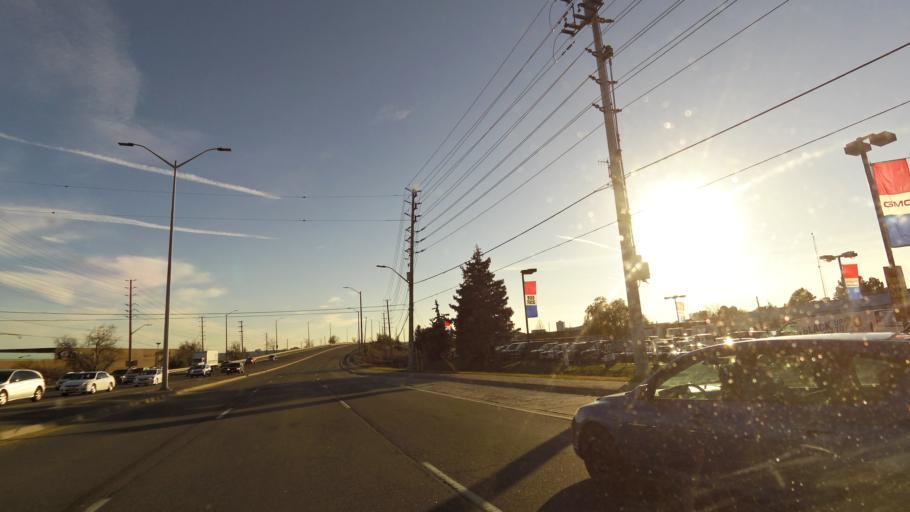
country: CA
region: Ontario
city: Mississauga
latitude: 43.5975
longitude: -79.7390
